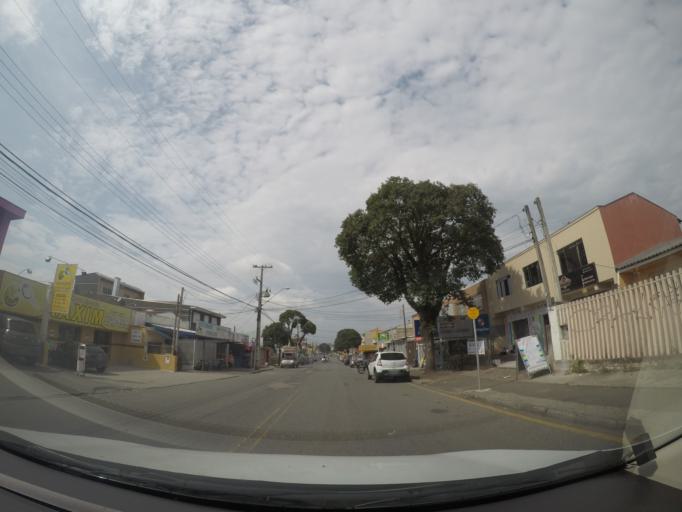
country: BR
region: Parana
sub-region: Sao Jose Dos Pinhais
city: Sao Jose dos Pinhais
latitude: -25.5140
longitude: -49.2781
